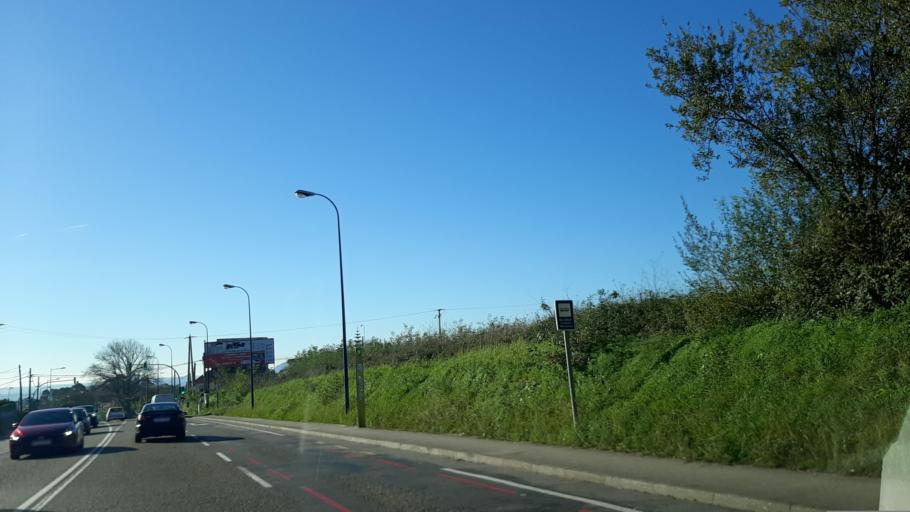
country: ES
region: Galicia
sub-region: Provincia de Pontevedra
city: Vigo
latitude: 42.2163
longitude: -8.7590
